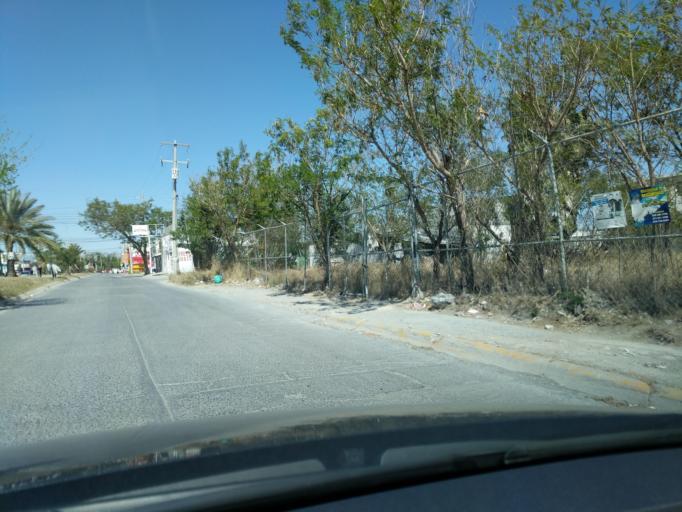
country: MX
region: Nuevo Leon
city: Juarez
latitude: 25.6356
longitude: -100.0870
